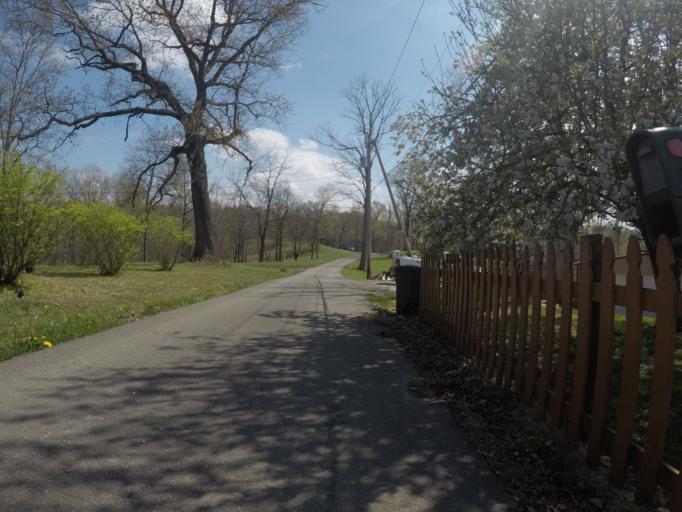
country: US
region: Ohio
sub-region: Lawrence County
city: Burlington
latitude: 38.3892
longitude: -82.5345
